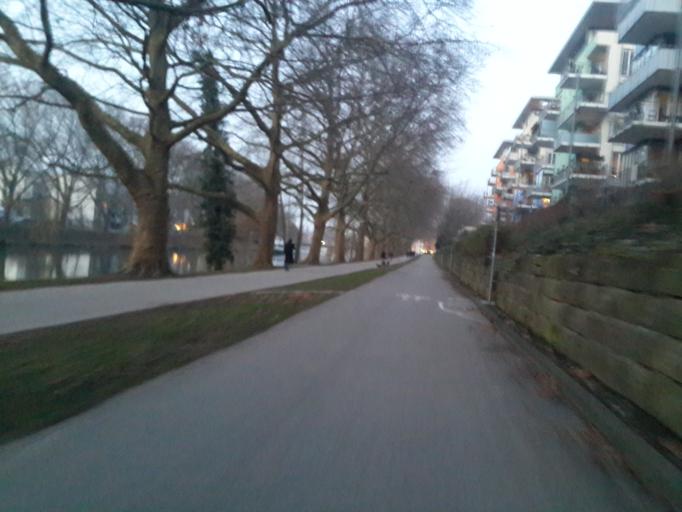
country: DE
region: Baden-Wuerttemberg
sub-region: Regierungsbezirk Stuttgart
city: Heilbronn
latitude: 49.1378
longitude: 9.2125
